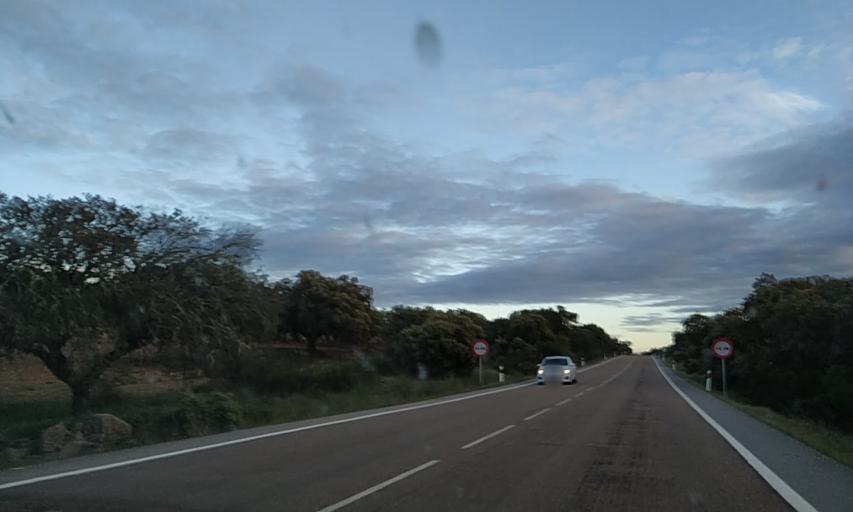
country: ES
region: Extremadura
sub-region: Provincia de Badajoz
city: Puebla de Obando
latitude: 39.2873
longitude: -6.5222
